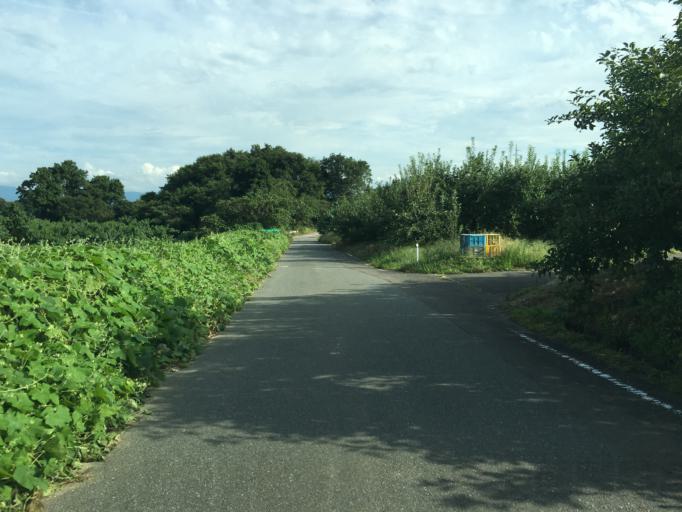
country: JP
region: Fukushima
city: Hobaramachi
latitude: 37.8349
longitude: 140.4699
